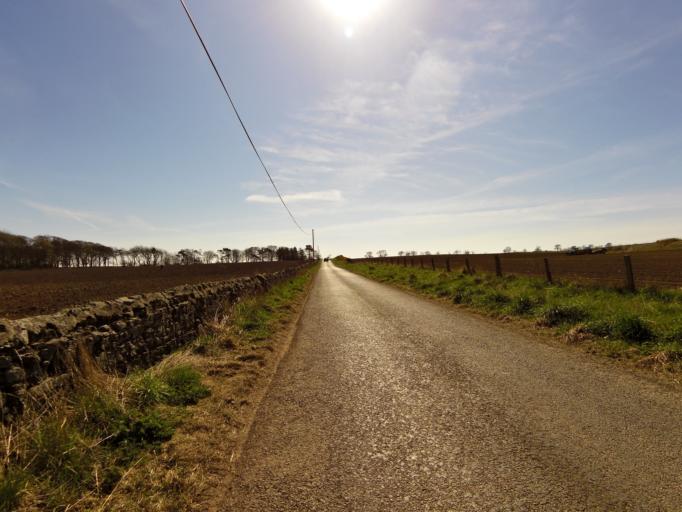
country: GB
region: Scotland
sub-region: Angus
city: Montrose
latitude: 56.6886
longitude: -2.4600
